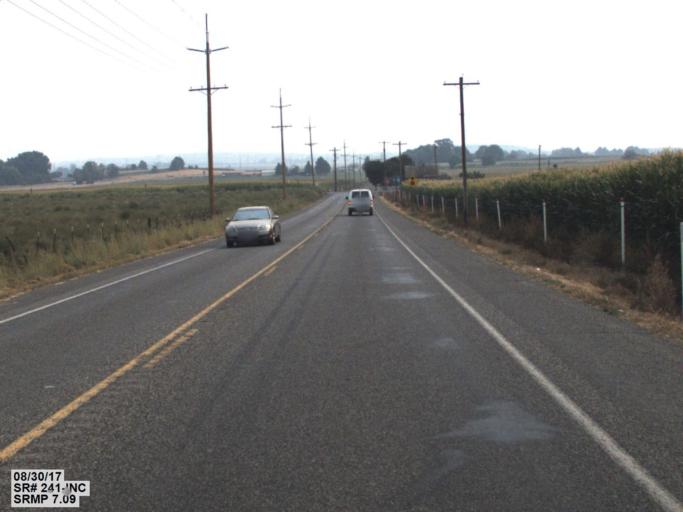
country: US
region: Washington
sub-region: Yakima County
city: Sunnyside
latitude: 46.3023
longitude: -119.9815
